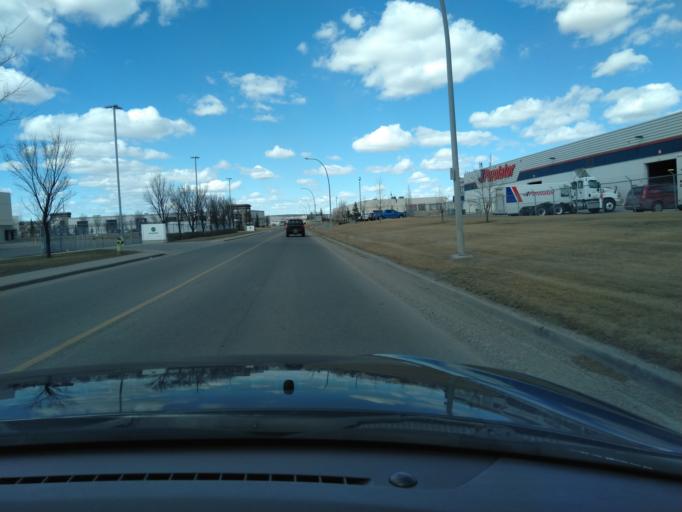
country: CA
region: Alberta
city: Calgary
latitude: 51.1201
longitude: -114.0343
